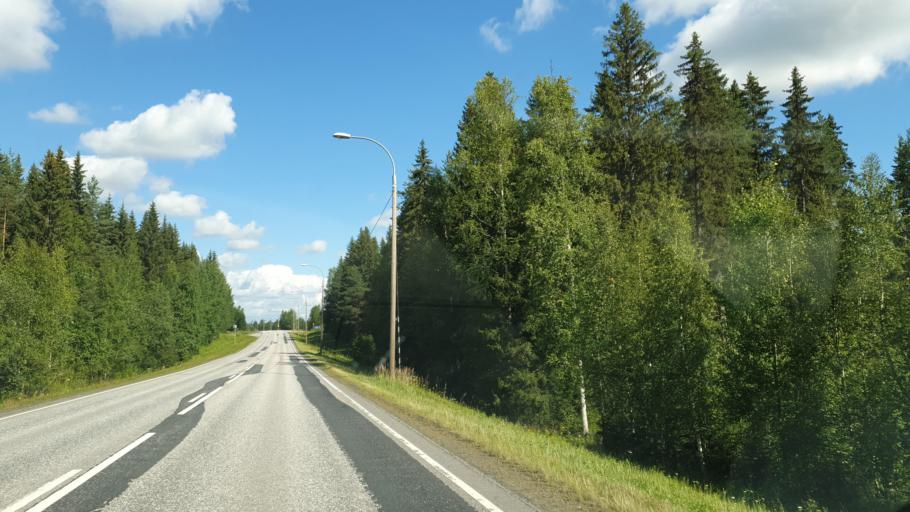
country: FI
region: Northern Savo
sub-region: Ylae-Savo
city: Sonkajaervi
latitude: 63.7230
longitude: 27.3703
